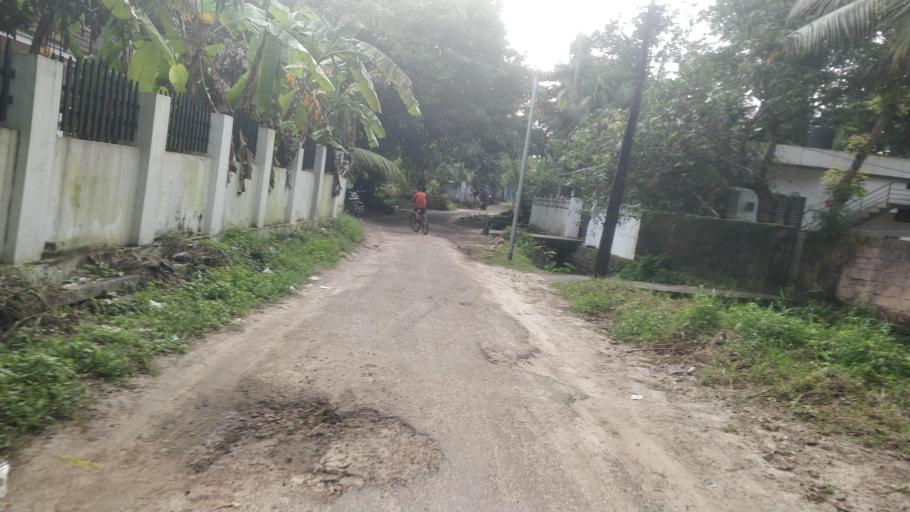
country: IN
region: Kerala
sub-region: Alappuzha
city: Vayalar
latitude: 9.6900
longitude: 76.3322
